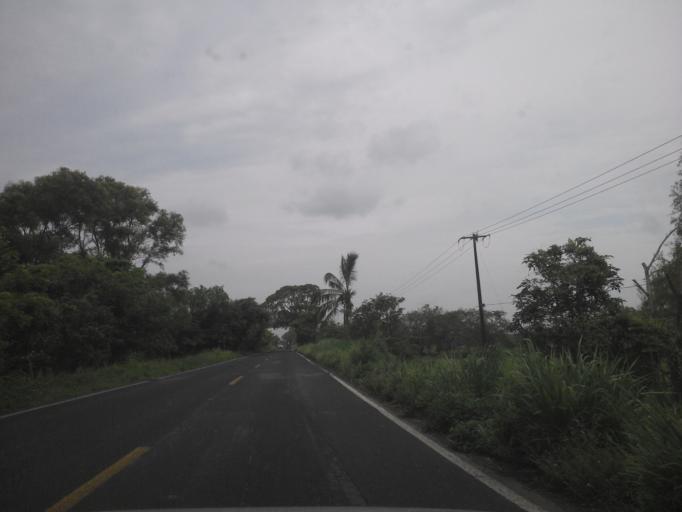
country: MX
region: Veracruz
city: Nautla
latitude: 20.2181
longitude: -96.7849
